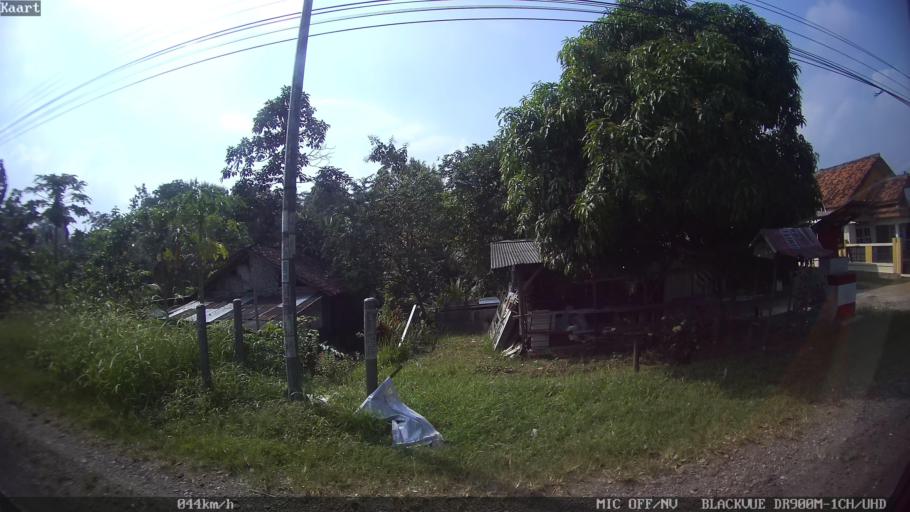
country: ID
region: Lampung
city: Gedongtataan
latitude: -5.3703
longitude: 105.1324
